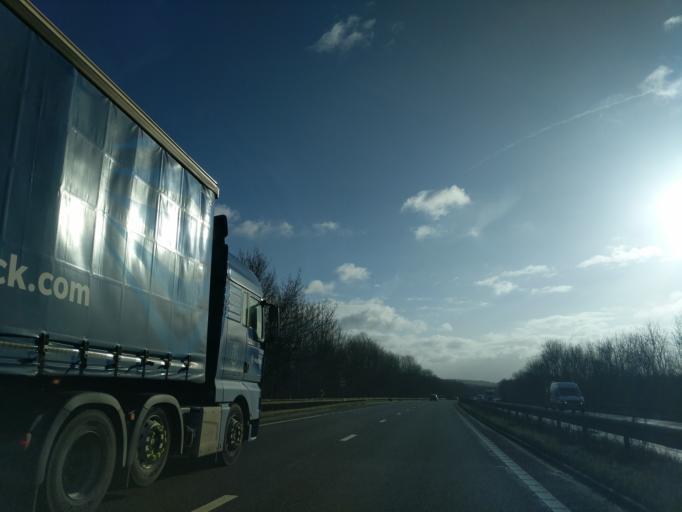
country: GB
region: England
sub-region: Derbyshire
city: Kilburn
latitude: 53.0064
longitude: -1.4456
